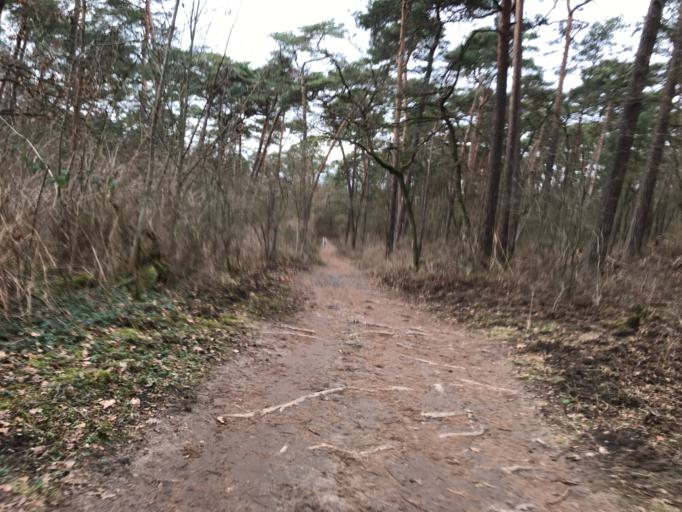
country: DE
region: Rheinland-Pfalz
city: Budenheim
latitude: 50.0131
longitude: 8.1948
